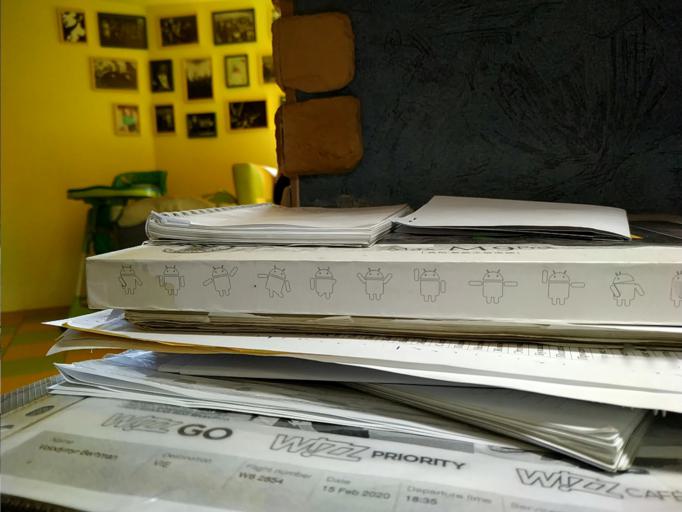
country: RU
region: Pskov
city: Plyussa
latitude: 58.5093
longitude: 29.5410
